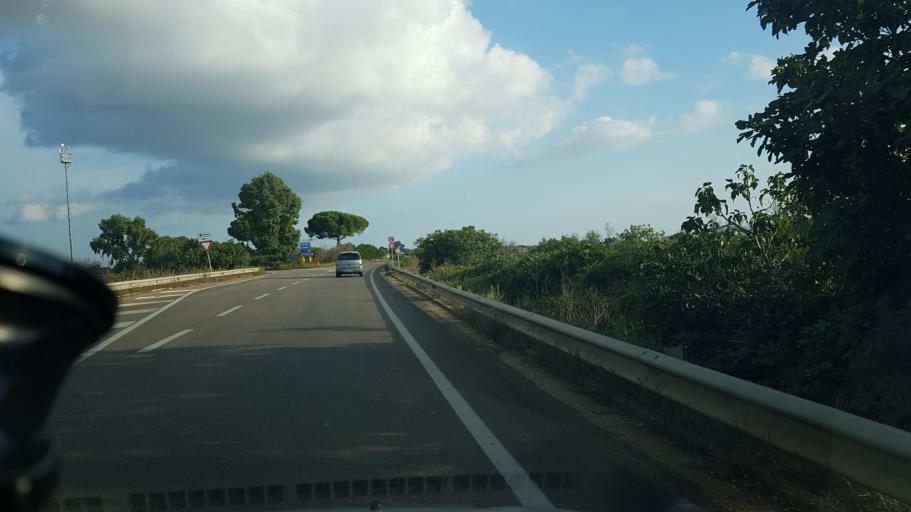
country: IT
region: Apulia
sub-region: Provincia di Lecce
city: Acquarica del Capo
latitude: 39.9132
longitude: 18.2317
